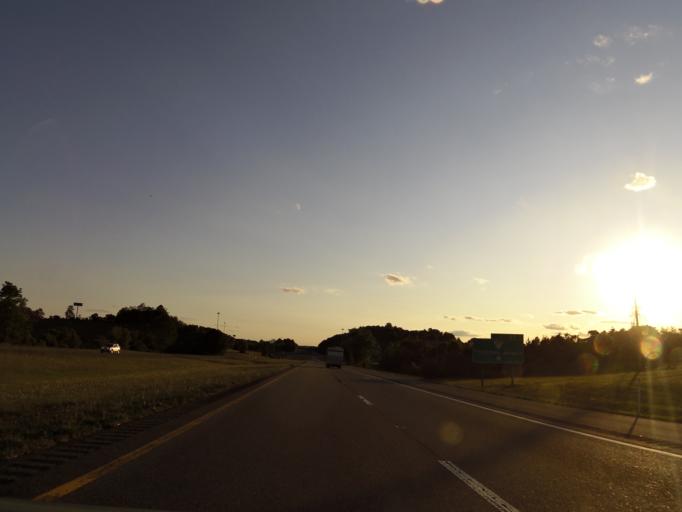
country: US
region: Tennessee
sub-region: Washington County
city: Spurgeon
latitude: 36.5094
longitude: -82.4250
